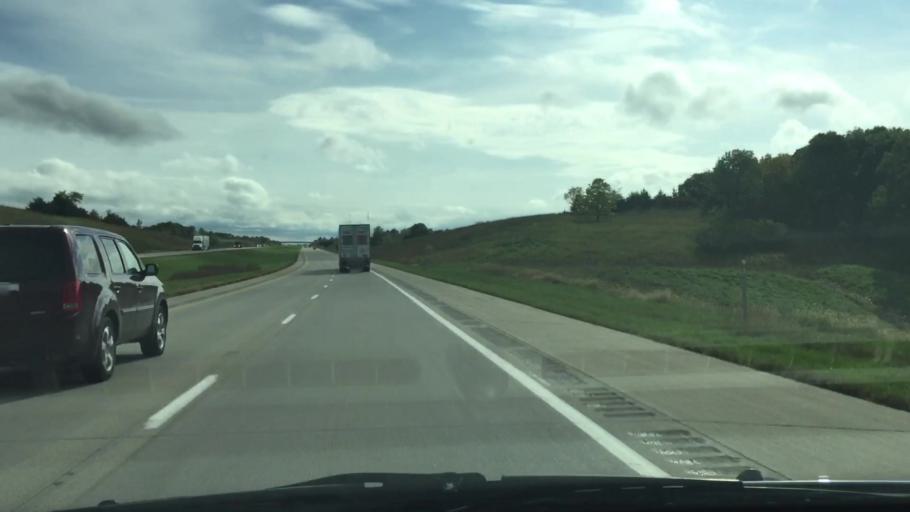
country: US
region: Iowa
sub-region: Clarke County
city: Osceola
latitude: 40.8885
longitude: -93.7975
